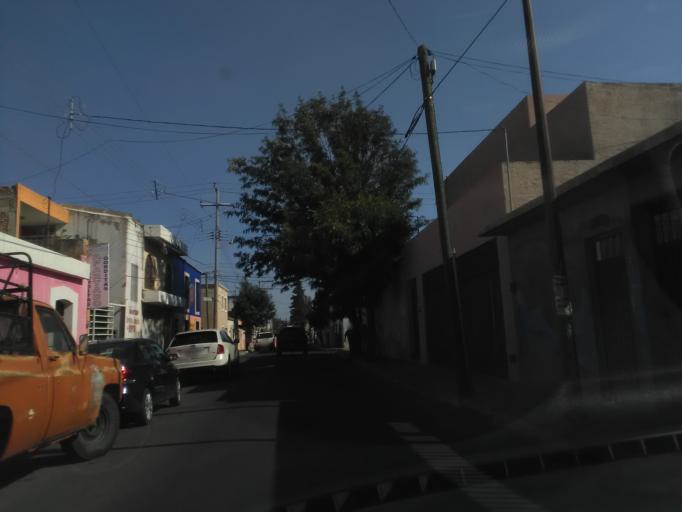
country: MX
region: Durango
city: Victoria de Durango
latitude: 24.0328
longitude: -104.6623
